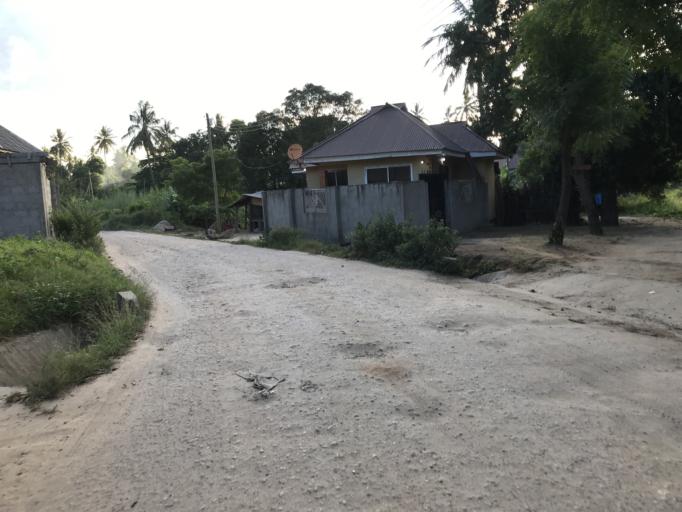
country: TZ
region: Dar es Salaam
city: Dar es Salaam
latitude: -6.8639
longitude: 39.3594
